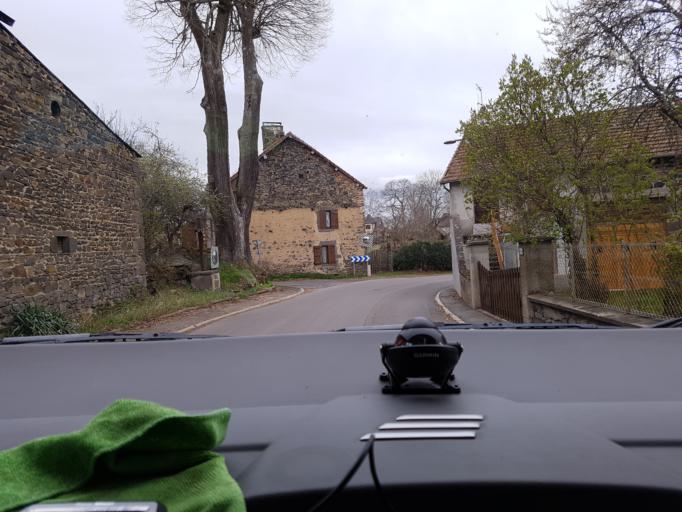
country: FR
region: Auvergne
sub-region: Departement du Puy-de-Dome
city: Chapdes-Beaufort
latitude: 45.8934
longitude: 2.8608
